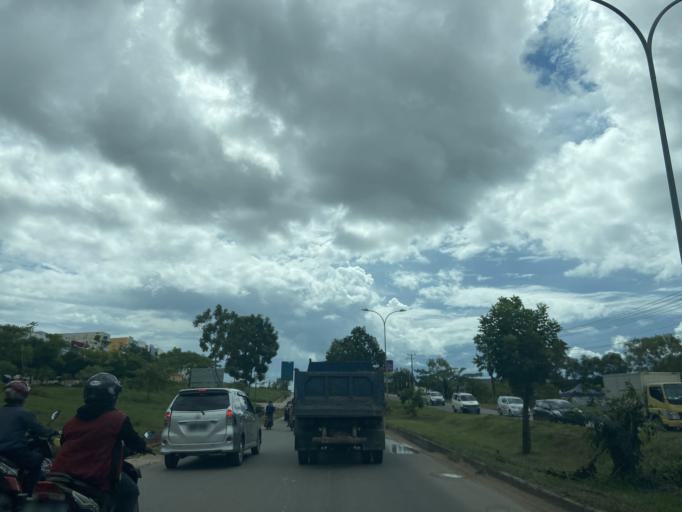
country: SG
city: Singapore
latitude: 1.0395
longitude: 103.9954
